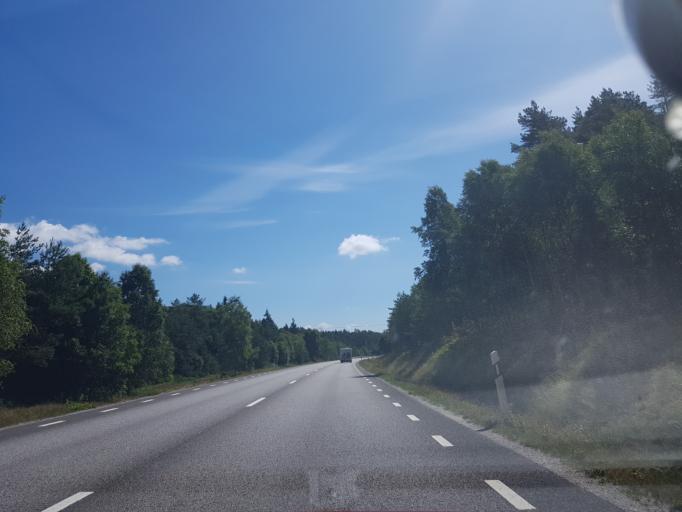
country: SE
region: Vaestra Goetaland
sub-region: Lysekils Kommun
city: Lysekil
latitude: 58.1572
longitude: 11.5115
